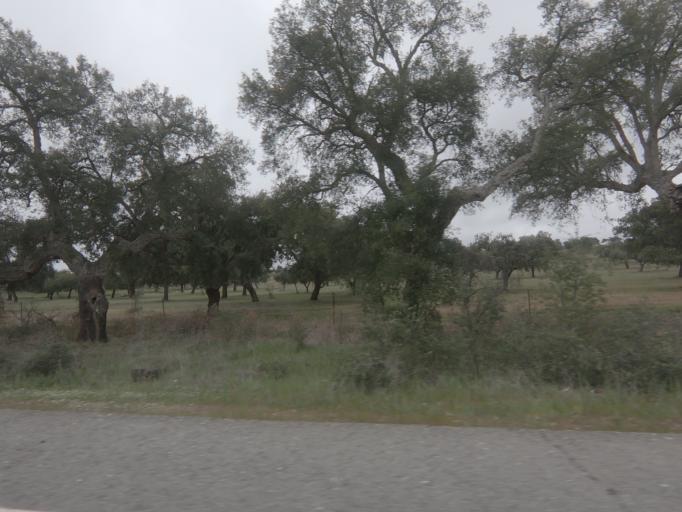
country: ES
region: Extremadura
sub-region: Provincia de Badajoz
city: Puebla de Obando
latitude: 39.2167
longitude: -6.5807
